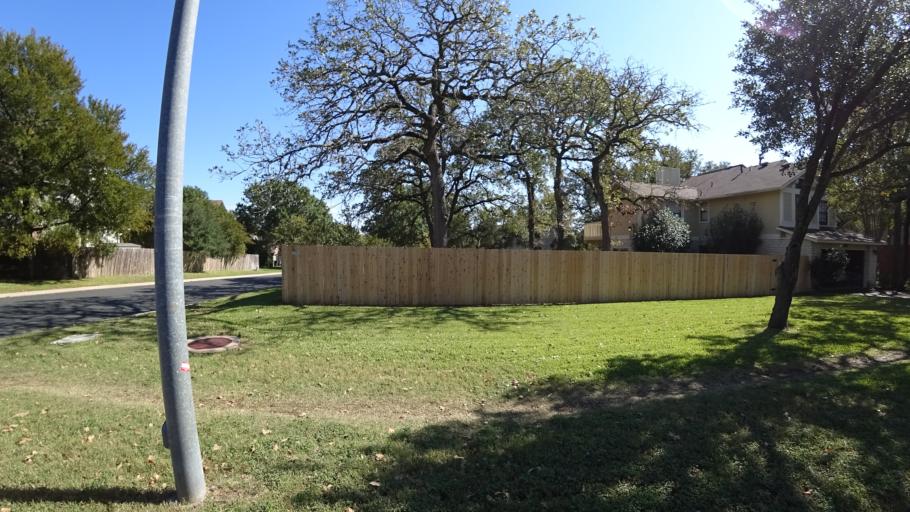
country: US
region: Texas
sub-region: Travis County
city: Shady Hollow
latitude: 30.2192
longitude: -97.8694
